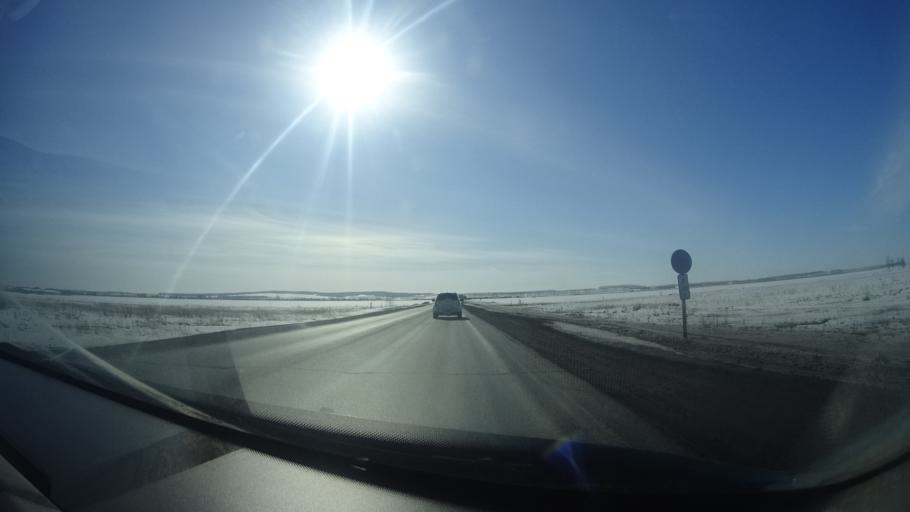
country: RU
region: Bashkortostan
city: Mikhaylovka
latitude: 54.8929
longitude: 55.7213
